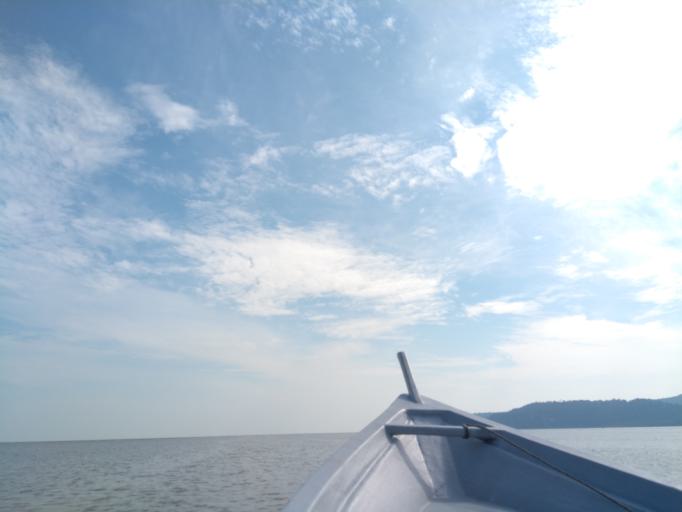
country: MY
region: Sarawak
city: Kuching
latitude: 1.6978
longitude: 110.4286
